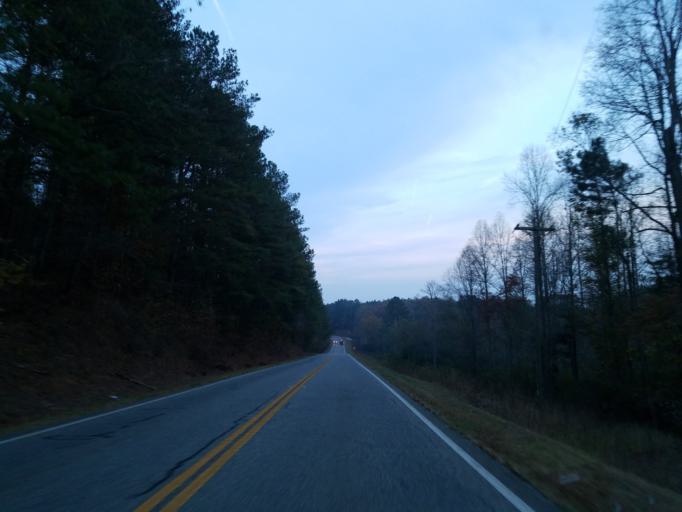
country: US
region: Georgia
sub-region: Gilmer County
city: Ellijay
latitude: 34.5665
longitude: -84.6102
